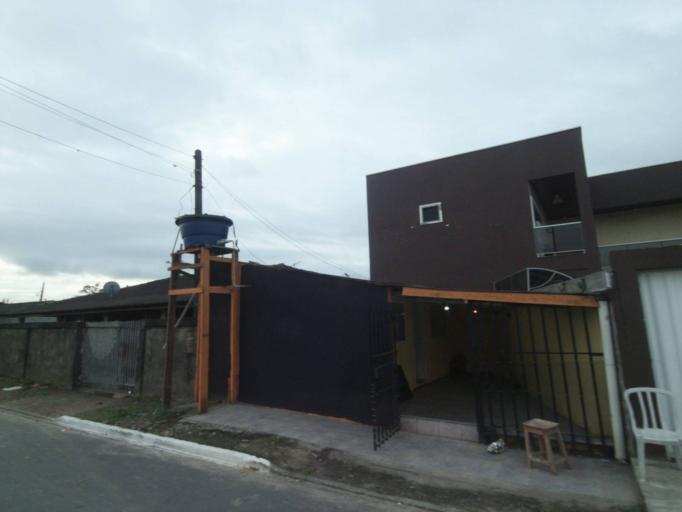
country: BR
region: Parana
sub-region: Paranagua
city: Paranagua
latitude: -25.5311
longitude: -48.5428
